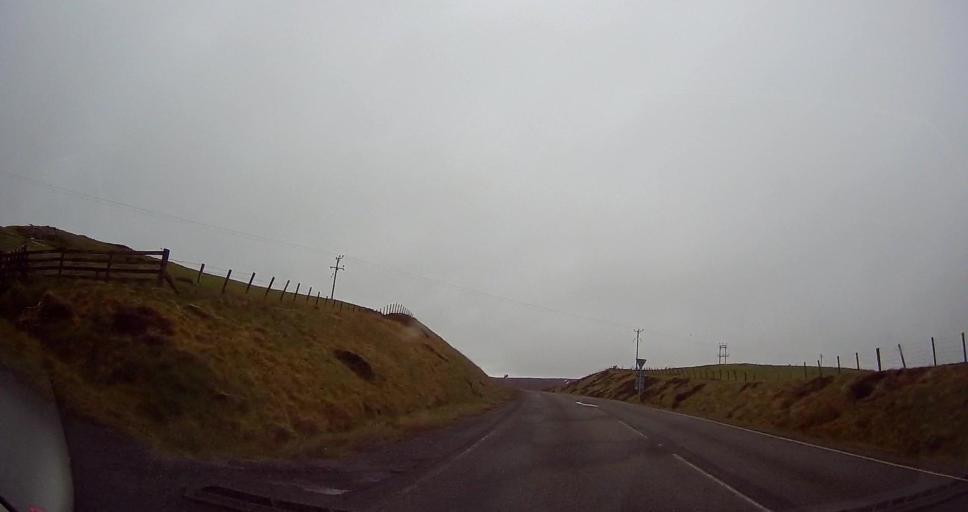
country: GB
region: Scotland
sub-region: Shetland Islands
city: Lerwick
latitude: 60.1381
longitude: -1.2164
